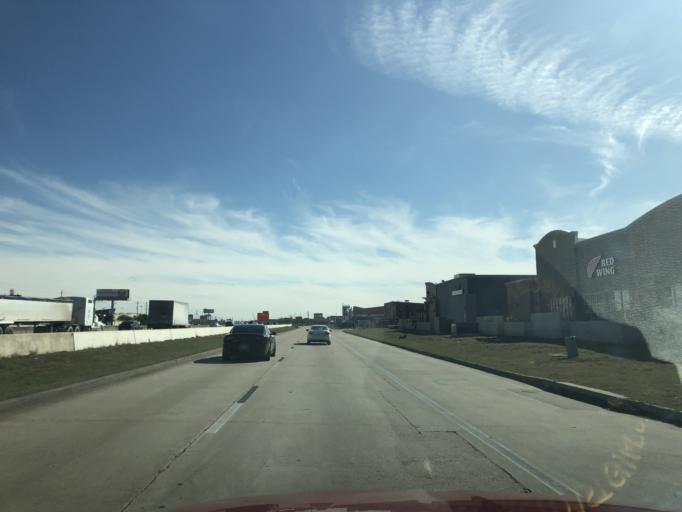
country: US
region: Texas
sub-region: Galveston County
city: League City
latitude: 29.4752
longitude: -95.0978
